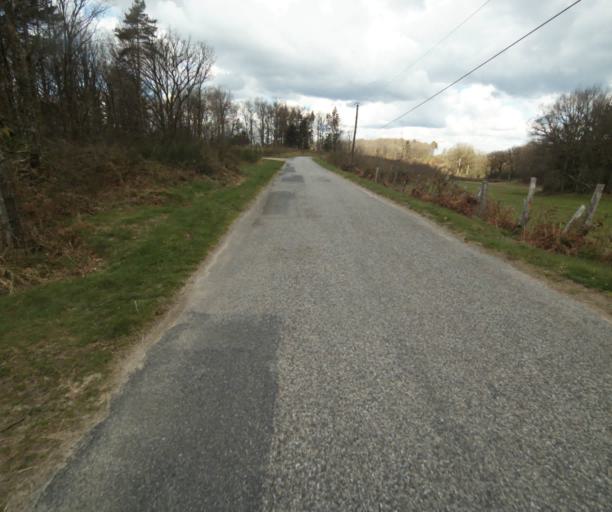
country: FR
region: Limousin
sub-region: Departement de la Correze
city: Correze
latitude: 45.2676
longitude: 1.8980
